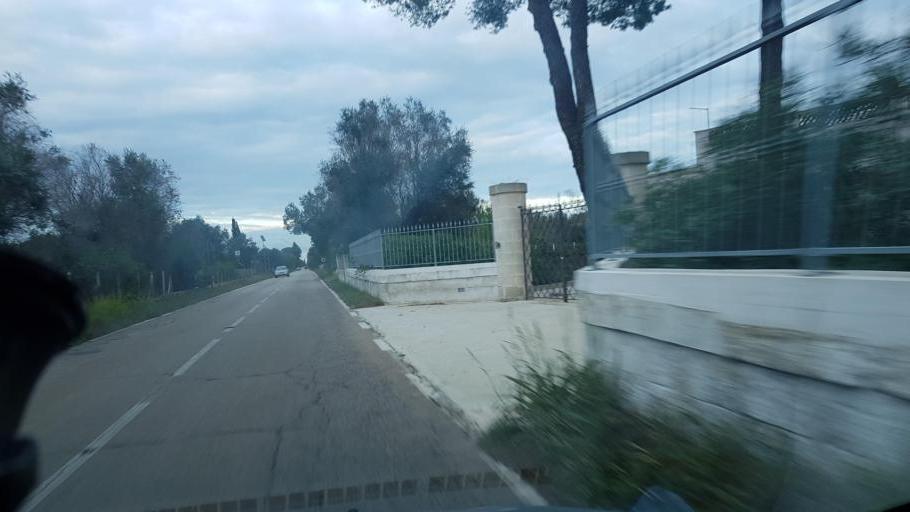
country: IT
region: Apulia
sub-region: Provincia di Brindisi
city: Oria
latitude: 40.5202
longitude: 17.6790
